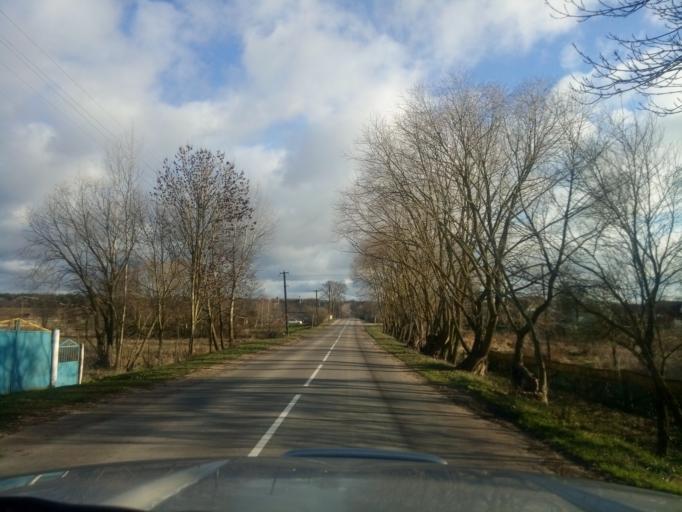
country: BY
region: Minsk
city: Tsimkavichy
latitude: 53.1755
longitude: 26.9617
